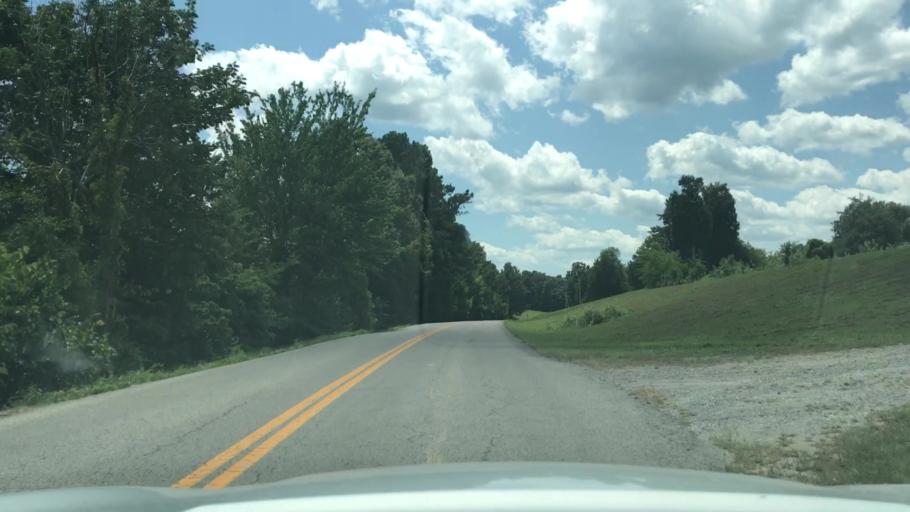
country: US
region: Kentucky
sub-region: Muhlenberg County
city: Greenville
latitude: 37.1398
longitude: -87.2641
